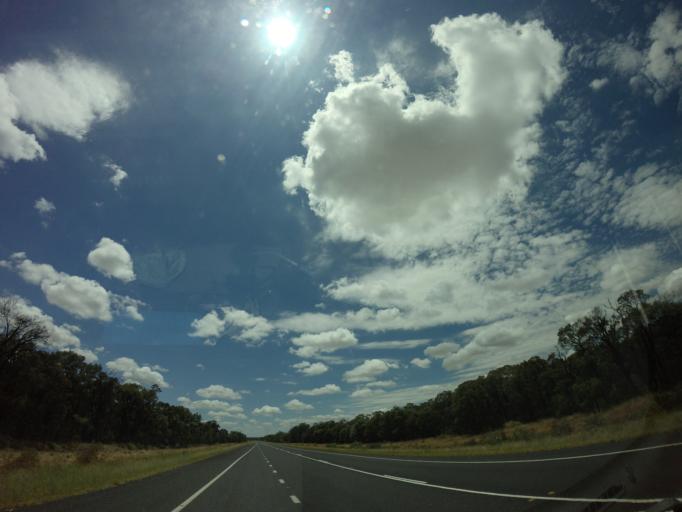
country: AU
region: New South Wales
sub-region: Moree Plains
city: Boggabilla
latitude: -28.8647
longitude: 150.1994
